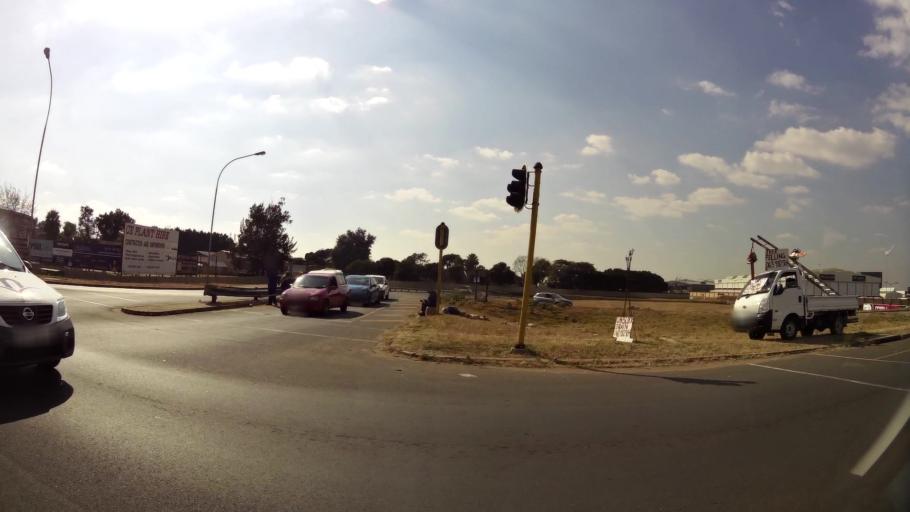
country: ZA
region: Gauteng
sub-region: City of Johannesburg Metropolitan Municipality
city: Modderfontein
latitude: -26.0992
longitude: 28.2523
